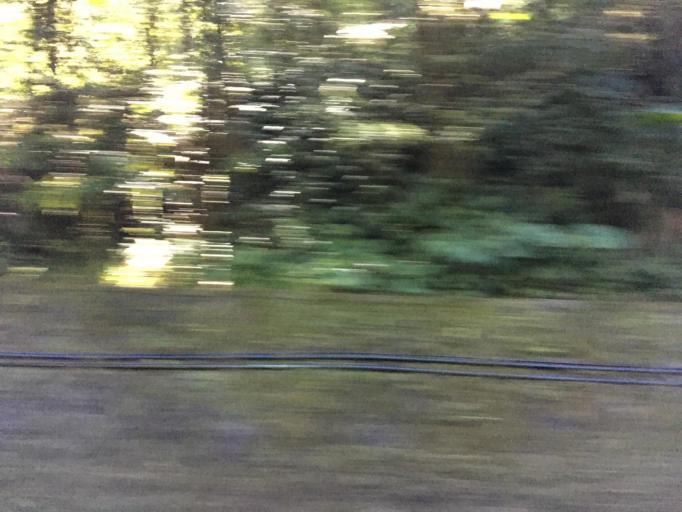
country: TW
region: Taiwan
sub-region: Yilan
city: Yilan
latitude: 24.5427
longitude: 121.5117
